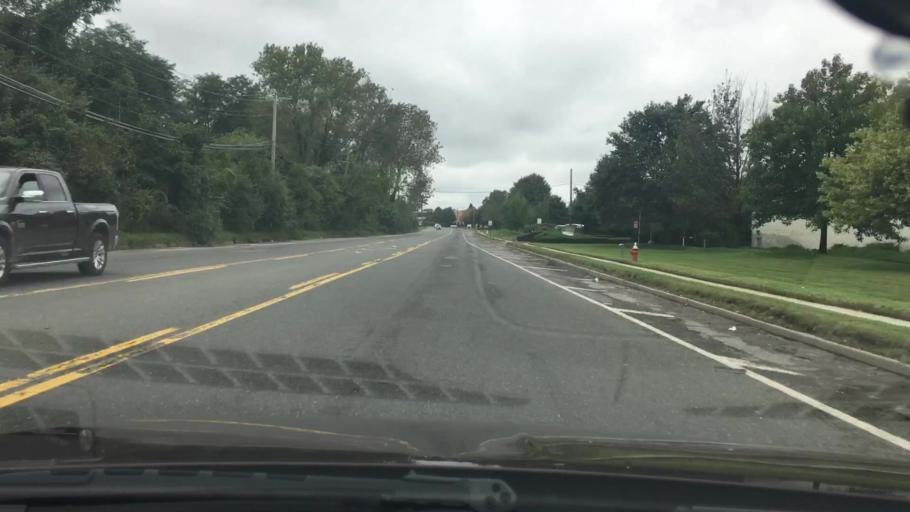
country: US
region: New York
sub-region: Nassau County
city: Old Bethpage
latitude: 40.7623
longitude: -73.4291
